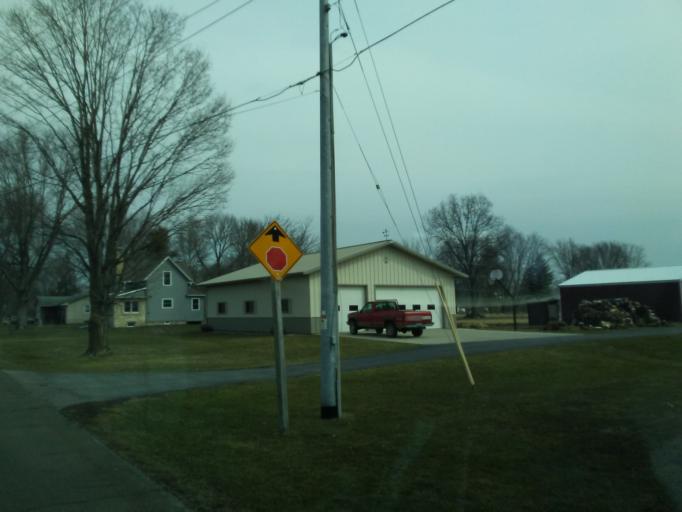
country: US
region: Wisconsin
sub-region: Columbia County
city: Lodi
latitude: 43.3257
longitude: -89.5318
